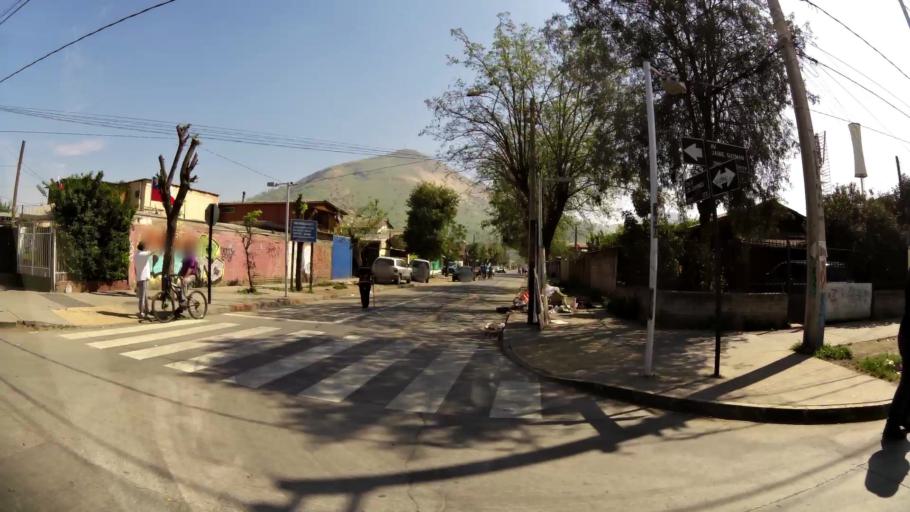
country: CL
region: Santiago Metropolitan
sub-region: Provincia de Santiago
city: Lo Prado
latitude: -33.4008
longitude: -70.6993
